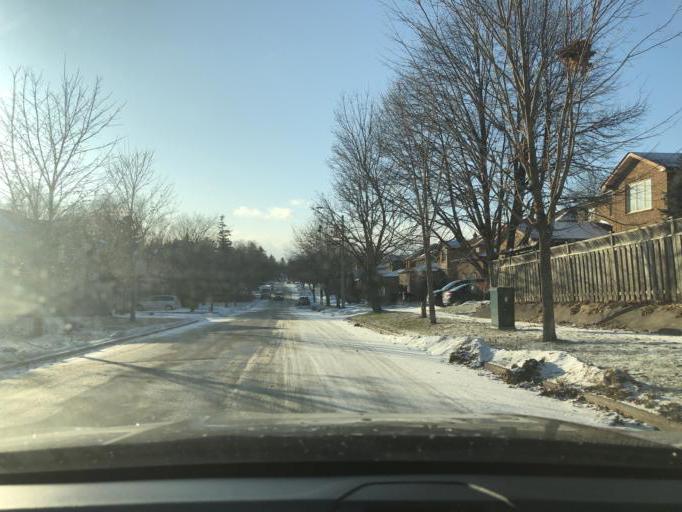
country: CA
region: Ontario
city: Scarborough
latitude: 43.7799
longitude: -79.1514
